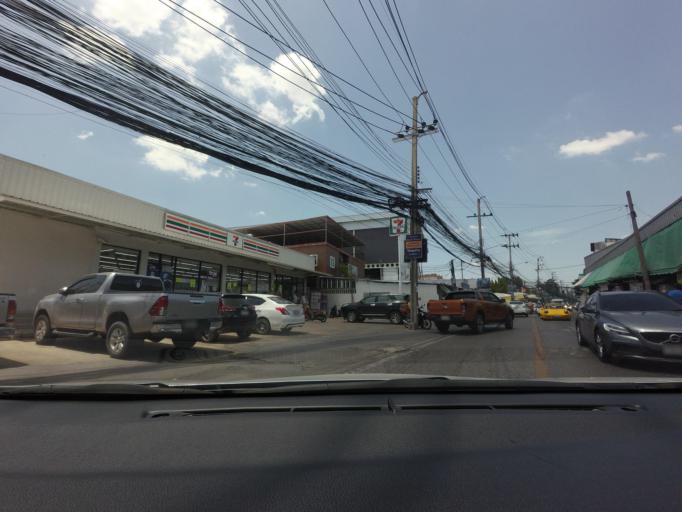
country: TH
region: Bangkok
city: Phra Khanong
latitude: 13.7272
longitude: 100.6167
